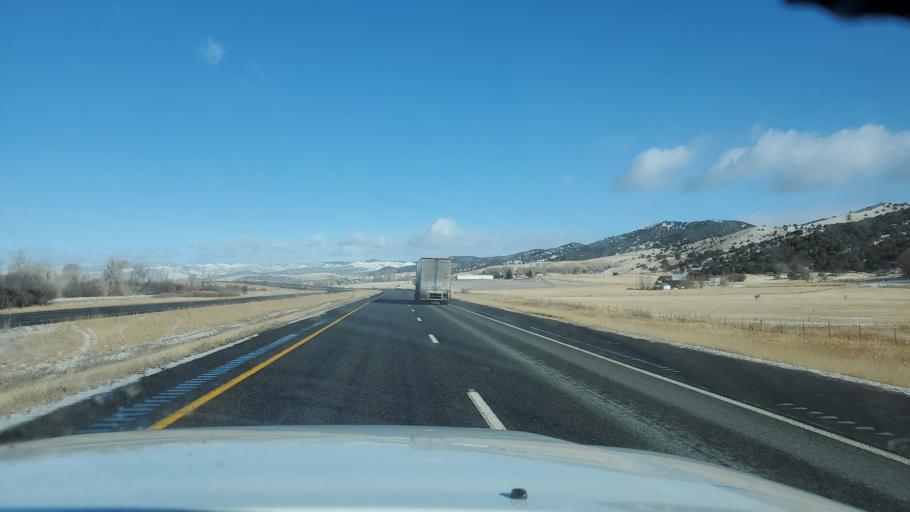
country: US
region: Utah
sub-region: Summit County
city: Coalville
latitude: 40.8368
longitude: -111.3907
